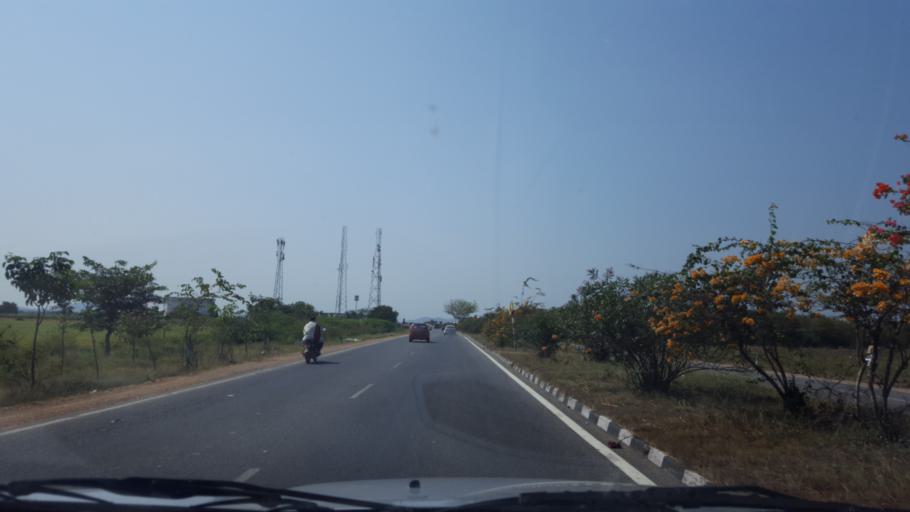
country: IN
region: Andhra Pradesh
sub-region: Guntur
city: Chilakalurupet
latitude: 16.0507
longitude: 80.1426
